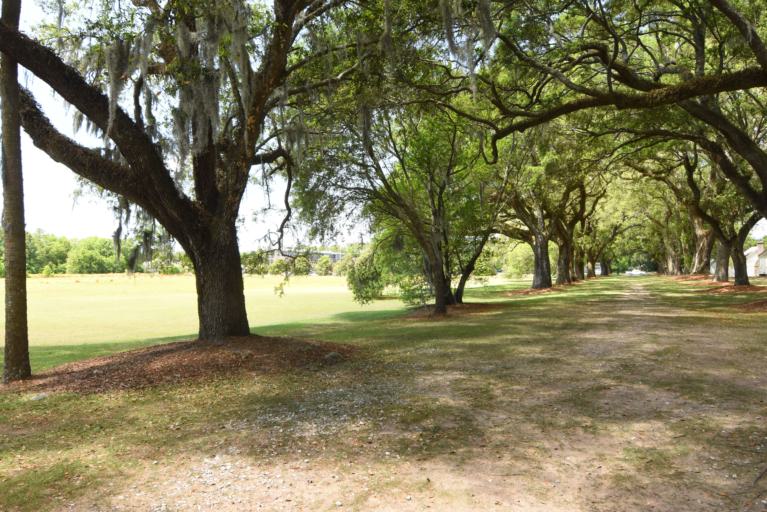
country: US
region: South Carolina
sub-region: Charleston County
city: Charleston
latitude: 32.7627
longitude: -79.9728
